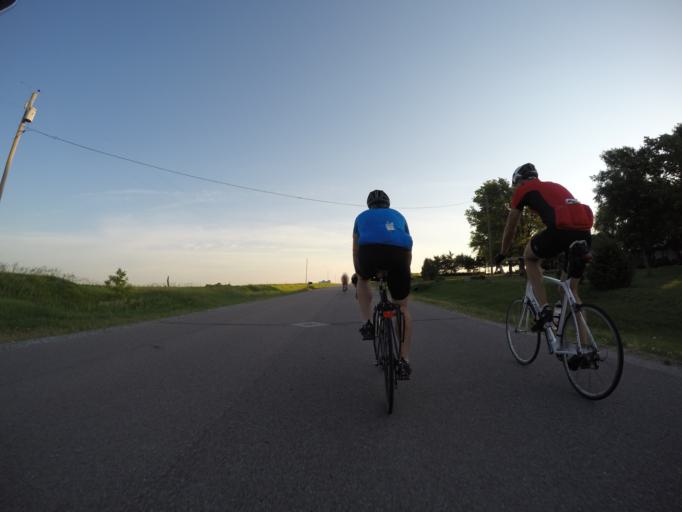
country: US
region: Kansas
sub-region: Marshall County
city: Marysville
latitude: 39.8490
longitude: -96.6009
